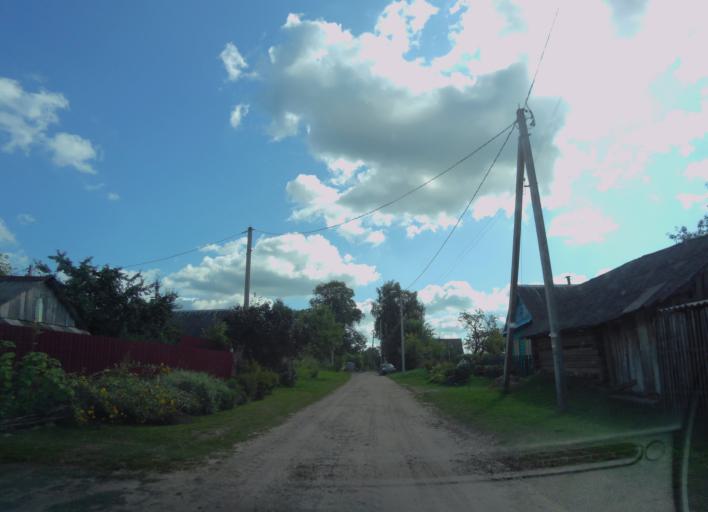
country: BY
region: Minsk
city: Zyembin
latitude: 54.3776
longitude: 28.3692
